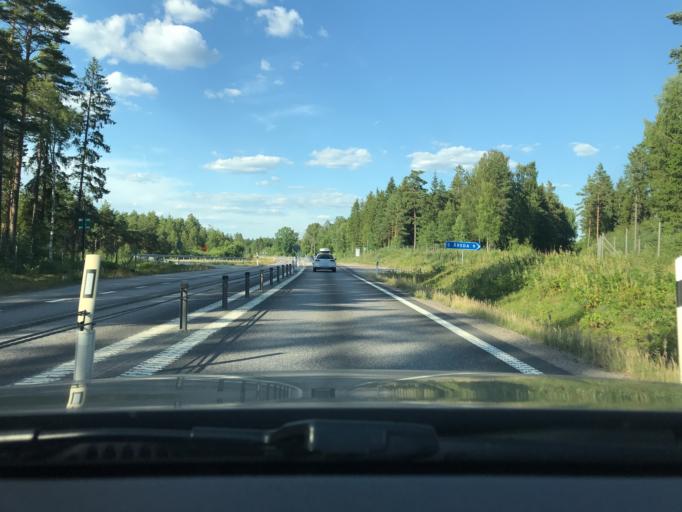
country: SE
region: Kronoberg
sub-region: Vaxjo Kommun
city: Rottne
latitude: 56.9701
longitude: 14.9736
